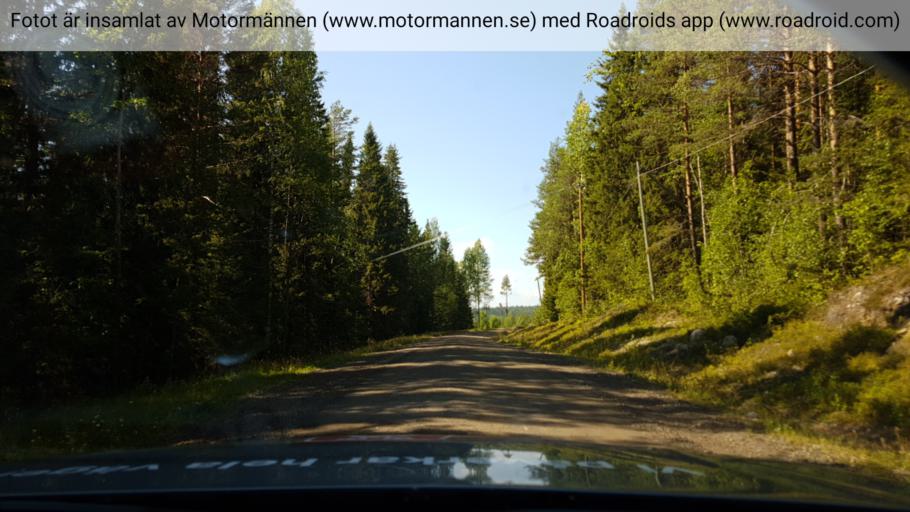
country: SE
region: Vaesterbotten
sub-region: Dorotea Kommun
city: Dorotea
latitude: 64.0859
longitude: 16.5390
